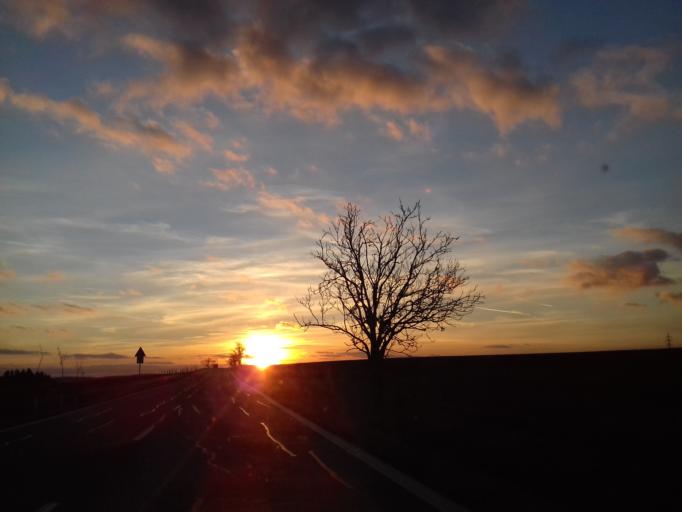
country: CZ
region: Vysocina
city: Krizova
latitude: 49.7054
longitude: 15.8383
